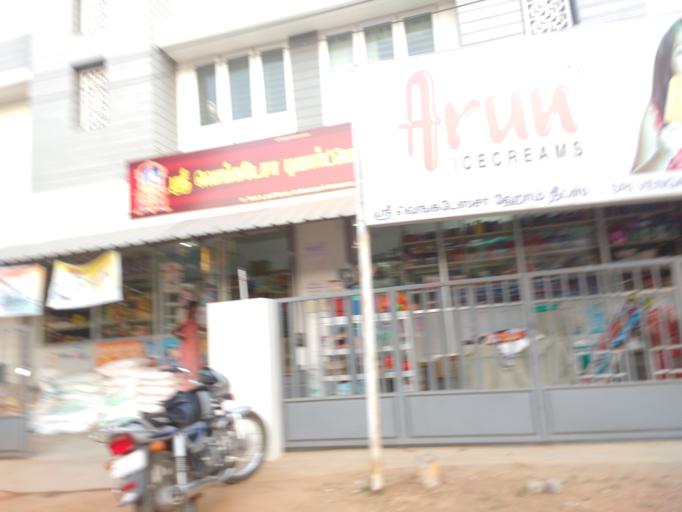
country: IN
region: Tamil Nadu
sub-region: Tiruppur
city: Udumalaippettai
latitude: 10.5538
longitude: 77.2312
